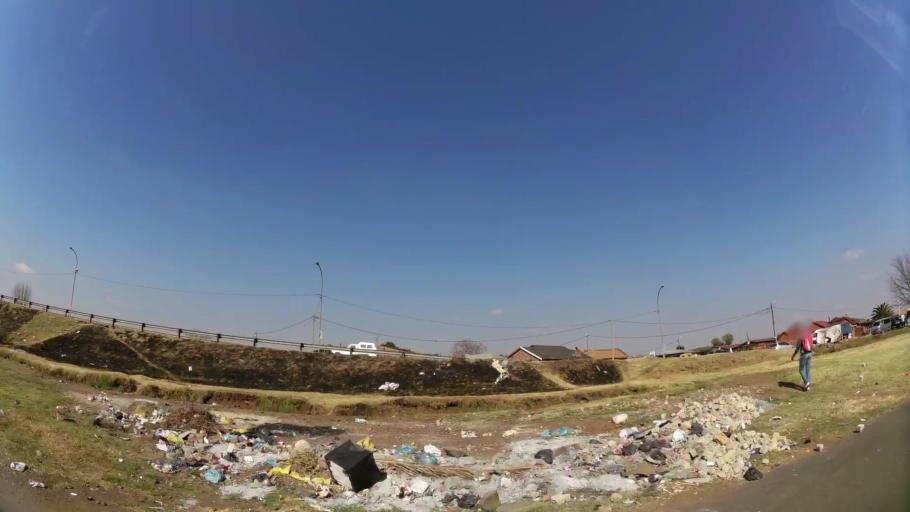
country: ZA
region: Gauteng
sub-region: Ekurhuleni Metropolitan Municipality
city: Boksburg
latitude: -26.2143
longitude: 28.2935
